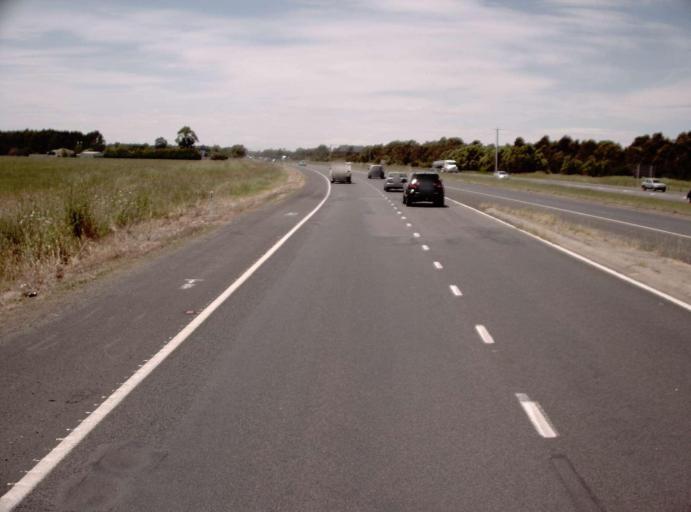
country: AU
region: Victoria
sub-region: Latrobe
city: Morwell
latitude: -38.2275
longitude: 146.4610
